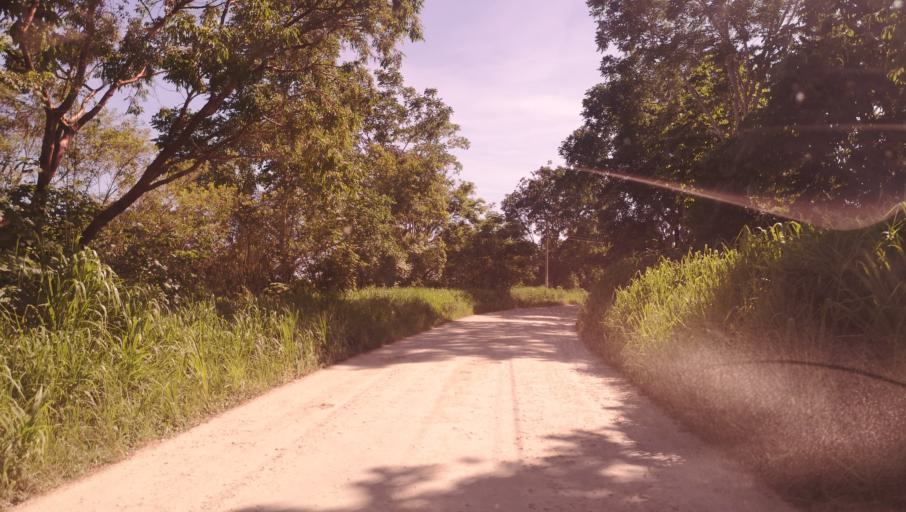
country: GT
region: Peten
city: Dolores
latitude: 16.7216
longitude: -89.3596
